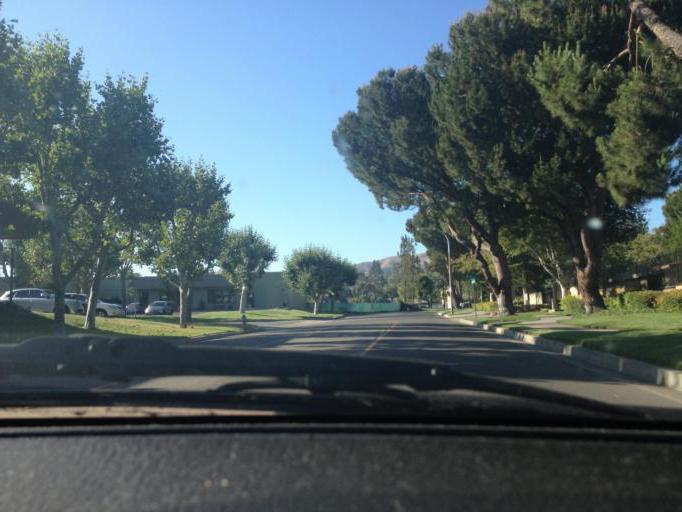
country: US
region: California
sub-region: Orange County
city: Brea
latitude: 33.9291
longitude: -117.9001
